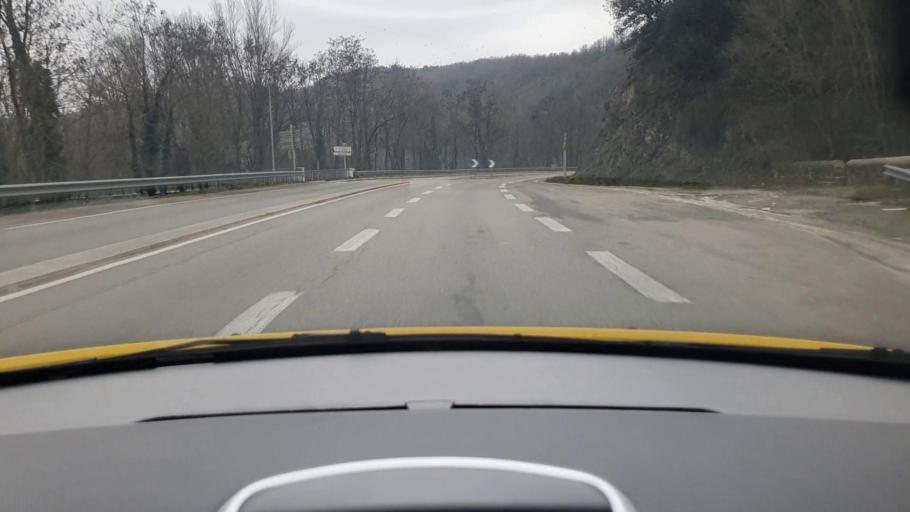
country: FR
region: Languedoc-Roussillon
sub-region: Departement du Gard
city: Molieres-sur-Ceze
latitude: 44.2662
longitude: 4.1535
